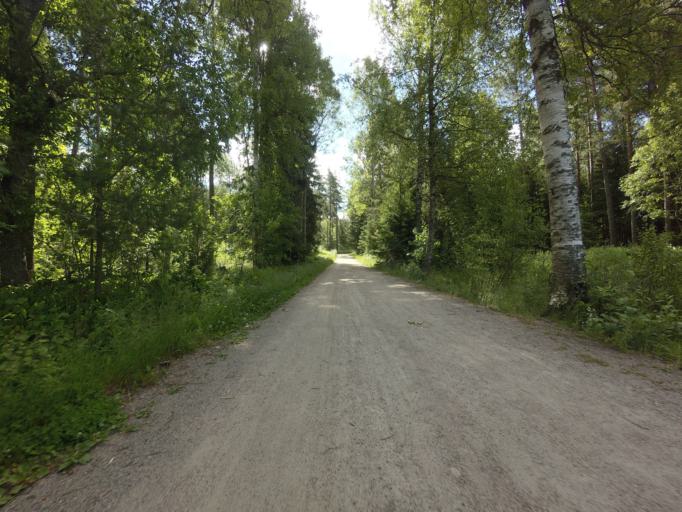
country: FI
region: Uusimaa
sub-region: Helsinki
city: Espoo
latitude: 60.1832
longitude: 24.6451
